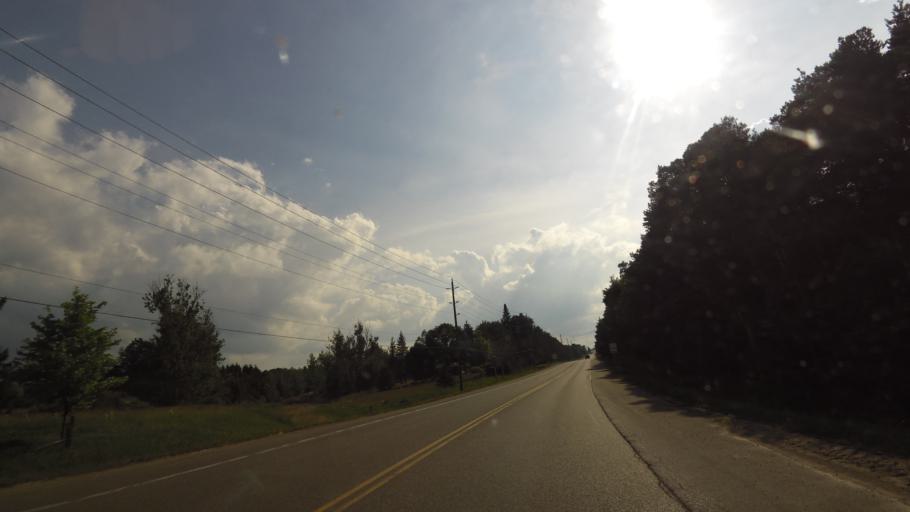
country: CA
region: Ontario
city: Orangeville
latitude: 43.9492
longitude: -80.0904
